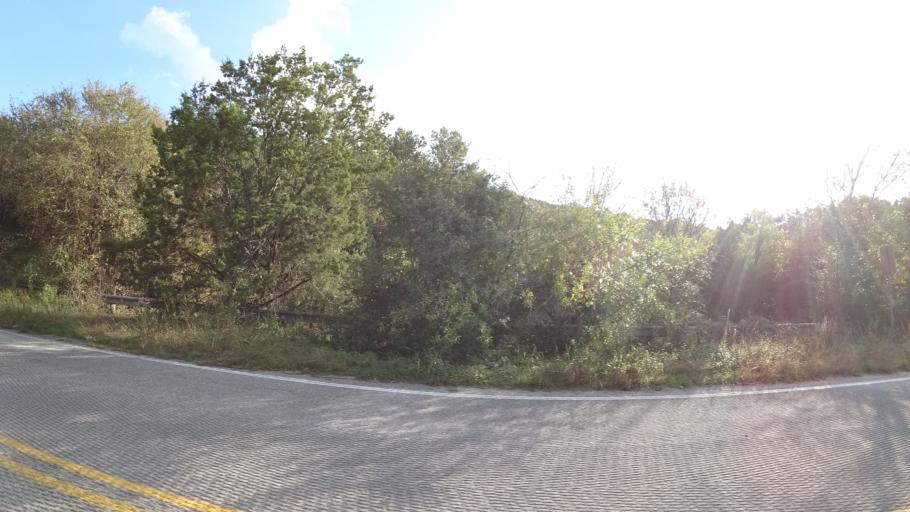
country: US
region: Texas
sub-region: Travis County
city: Barton Creek
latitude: 30.2724
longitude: -97.8551
